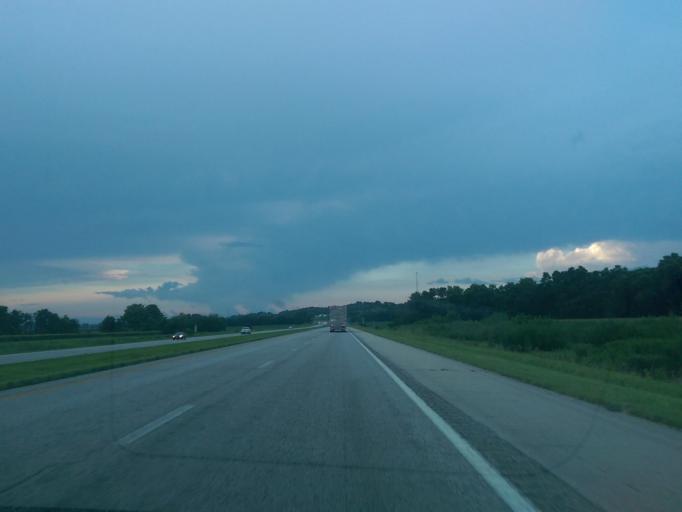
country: US
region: Missouri
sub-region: Holt County
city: Mound City
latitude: 40.0886
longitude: -95.2122
